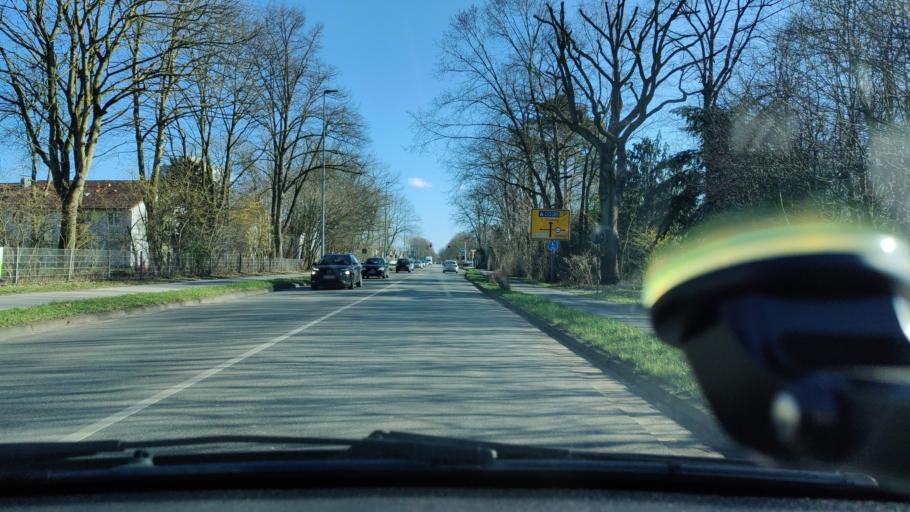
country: DE
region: North Rhine-Westphalia
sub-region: Regierungsbezirk Dusseldorf
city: Voerde
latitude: 51.6306
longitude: 6.6563
